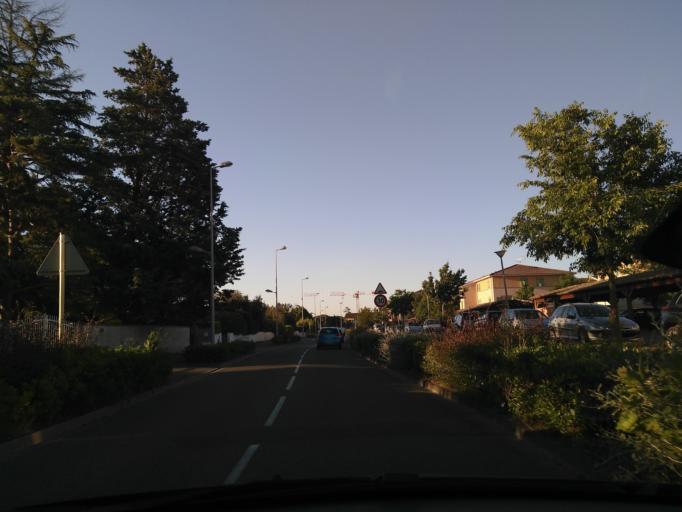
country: FR
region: Midi-Pyrenees
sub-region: Departement de la Haute-Garonne
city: Aussonne
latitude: 43.6875
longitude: 1.3207
